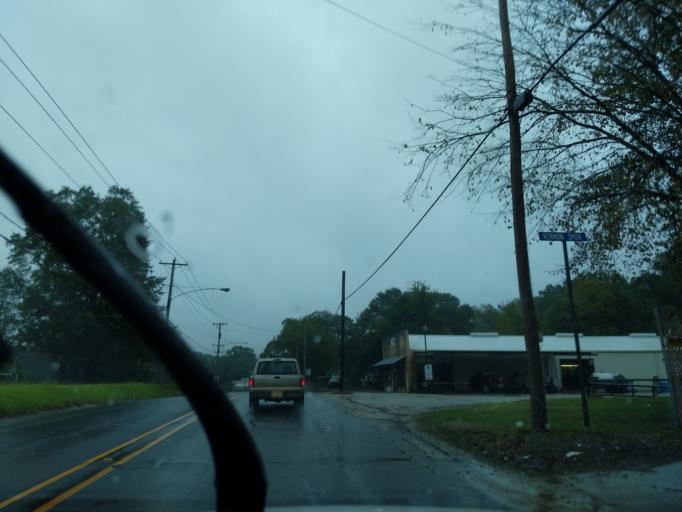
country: US
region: Texas
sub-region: Panola County
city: Carthage
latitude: 32.1576
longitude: -94.3335
